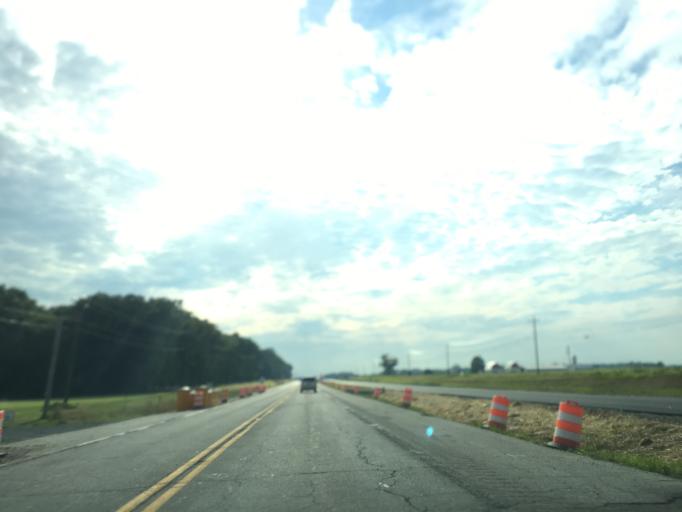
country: US
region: Maryland
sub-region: Caroline County
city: Ridgely
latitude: 38.9277
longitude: -75.9994
